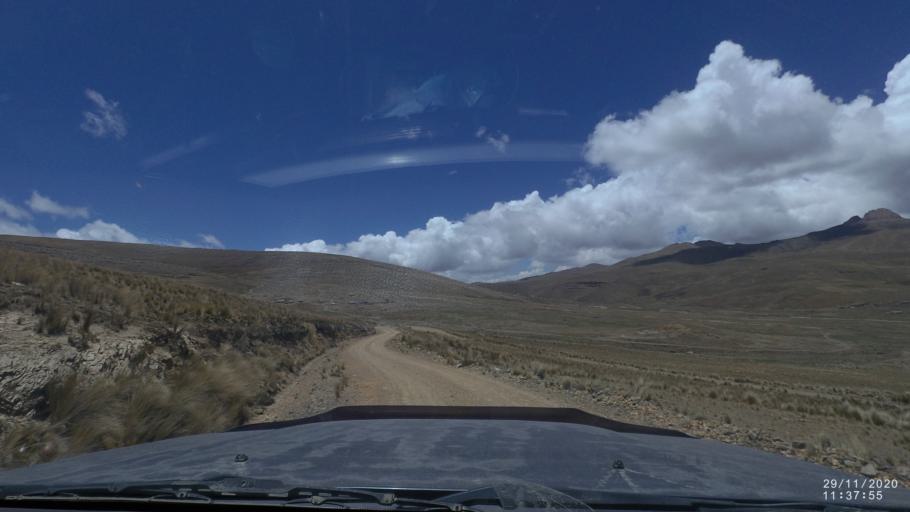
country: BO
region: Cochabamba
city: Cochabamba
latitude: -17.1986
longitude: -66.2344
